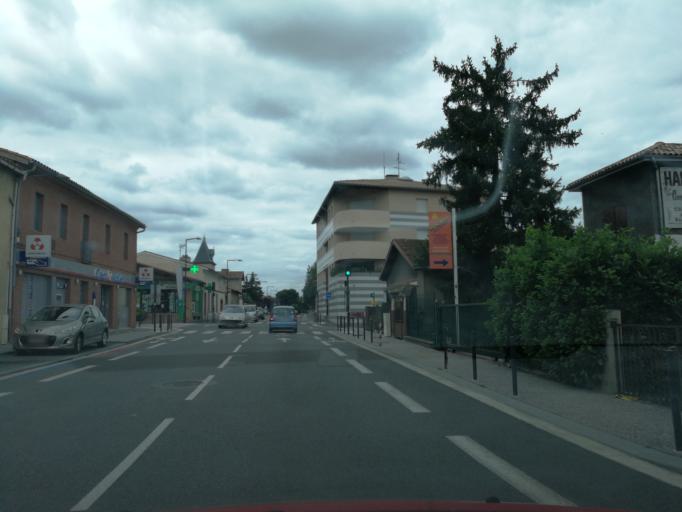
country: FR
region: Midi-Pyrenees
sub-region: Departement de la Haute-Garonne
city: Ramonville-Saint-Agne
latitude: 43.5465
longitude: 1.4740
